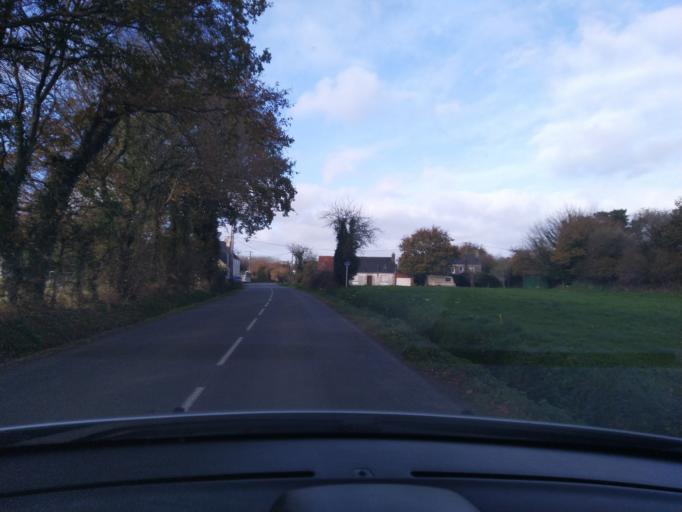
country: FR
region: Brittany
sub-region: Departement du Finistere
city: Plouigneau
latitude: 48.5475
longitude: -3.6840
